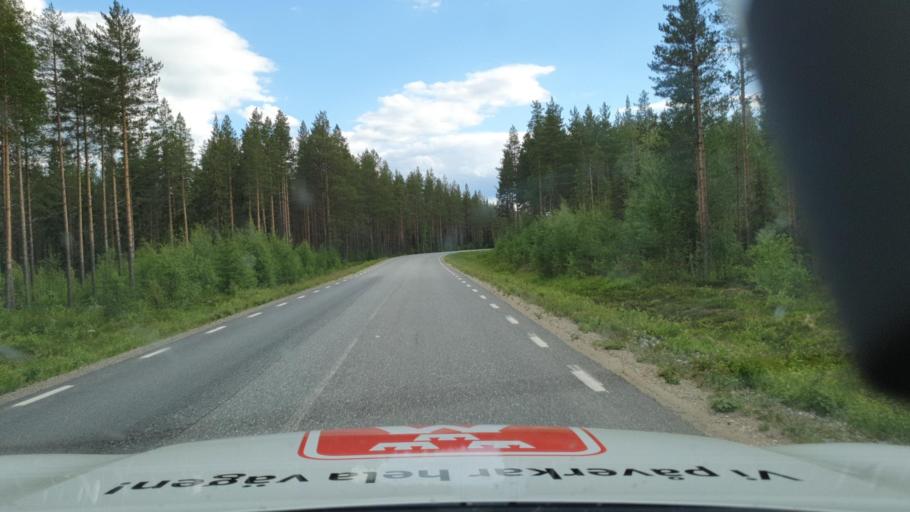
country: SE
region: Vaesterbotten
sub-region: Skelleftea Kommun
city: Langsele
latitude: 64.5946
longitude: 19.9330
